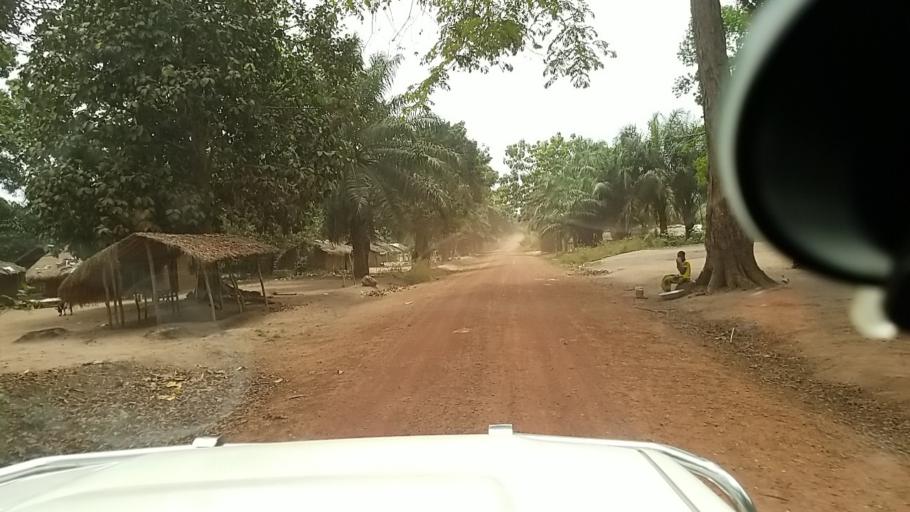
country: CD
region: Equateur
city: Libenge
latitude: 3.7433
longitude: 18.7837
